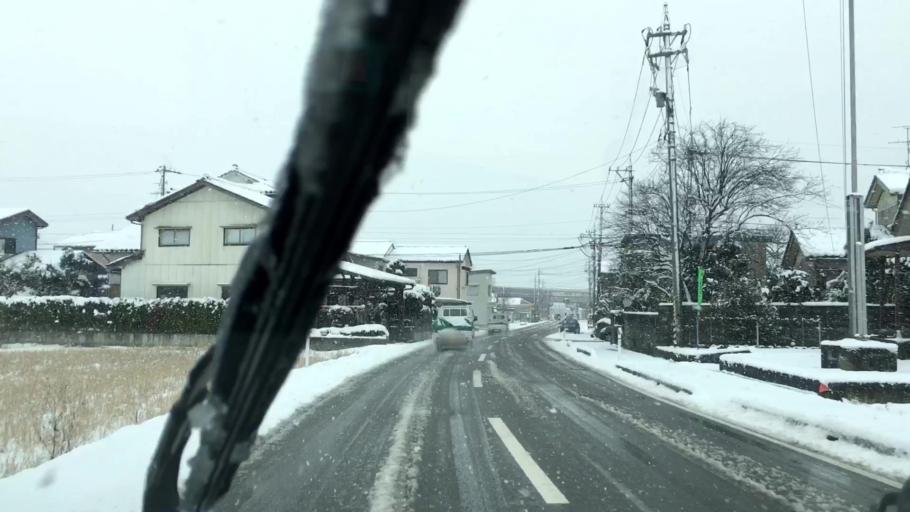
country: JP
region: Toyama
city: Kamiichi
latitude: 36.7001
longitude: 137.3354
